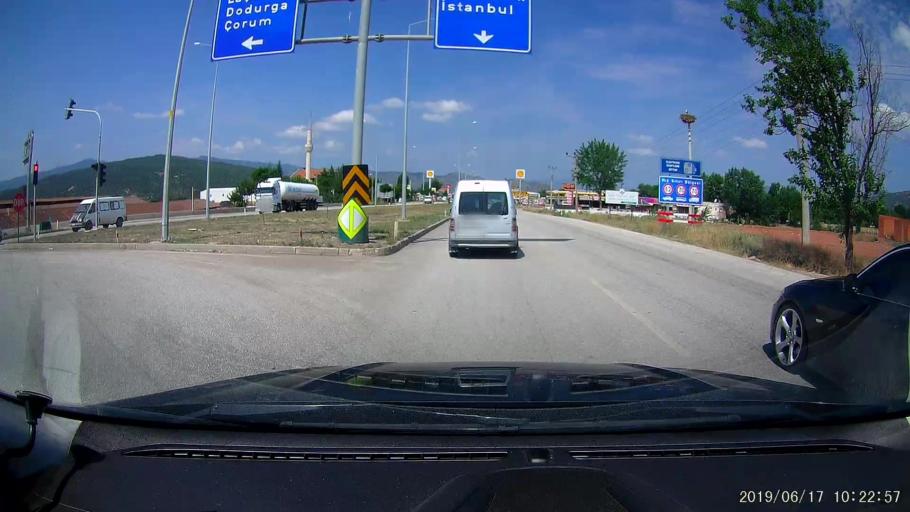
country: TR
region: Corum
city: Osmancik
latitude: 40.9711
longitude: 34.8452
